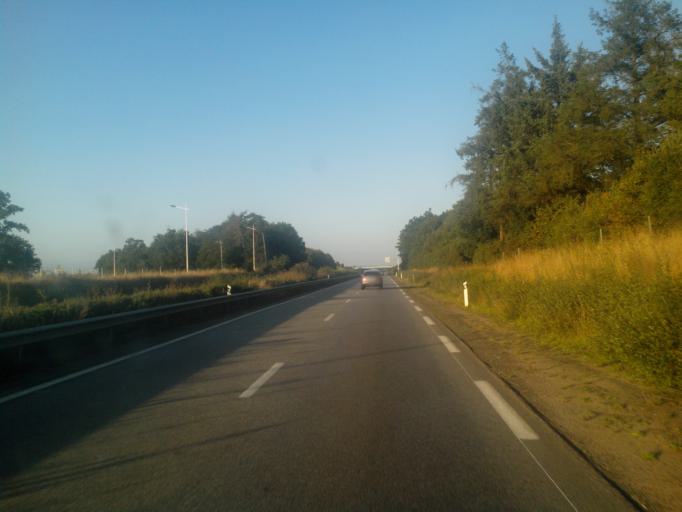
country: FR
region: Brittany
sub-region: Departement des Cotes-d'Armor
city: Loudeac
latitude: 48.1484
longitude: -2.7643
